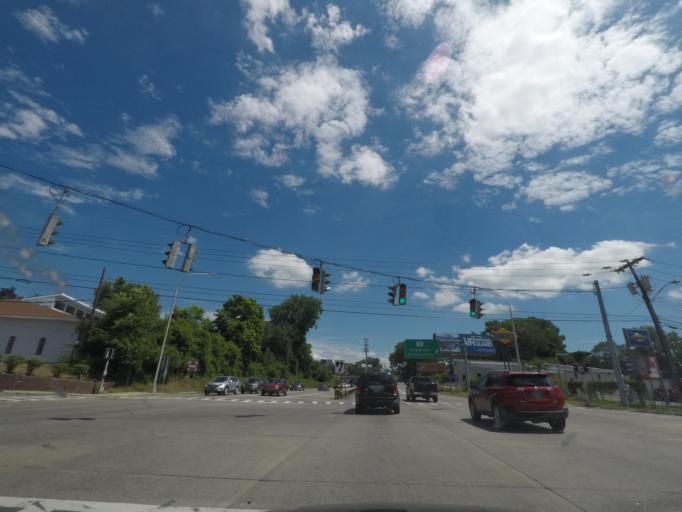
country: US
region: New York
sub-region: Schenectady County
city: Schenectady
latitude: 42.7842
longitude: -73.9128
